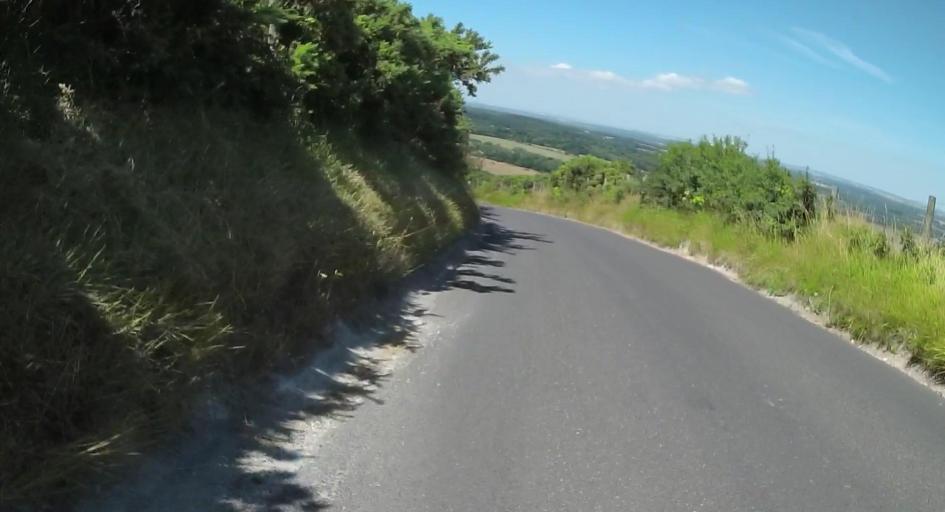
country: GB
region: England
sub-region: Dorset
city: Wool
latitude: 50.6307
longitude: -2.1707
